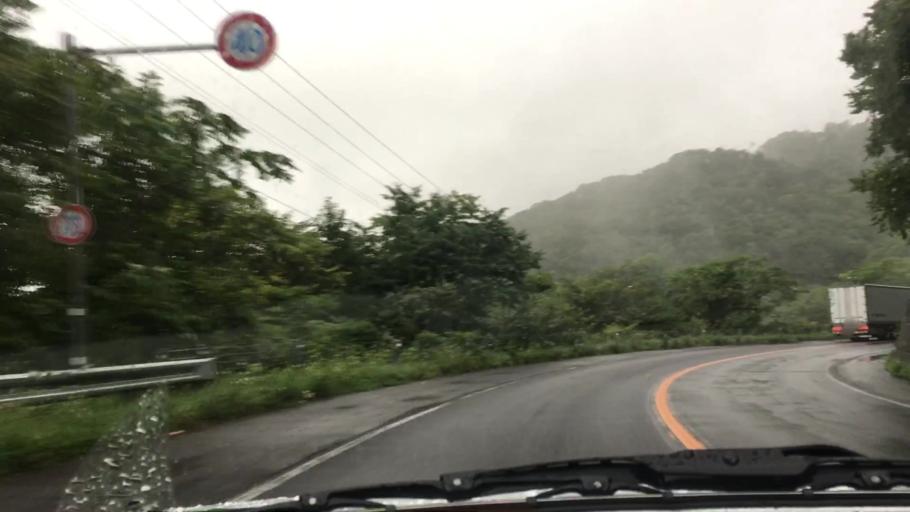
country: JP
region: Hokkaido
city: Niseko Town
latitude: 42.5919
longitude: 140.5913
